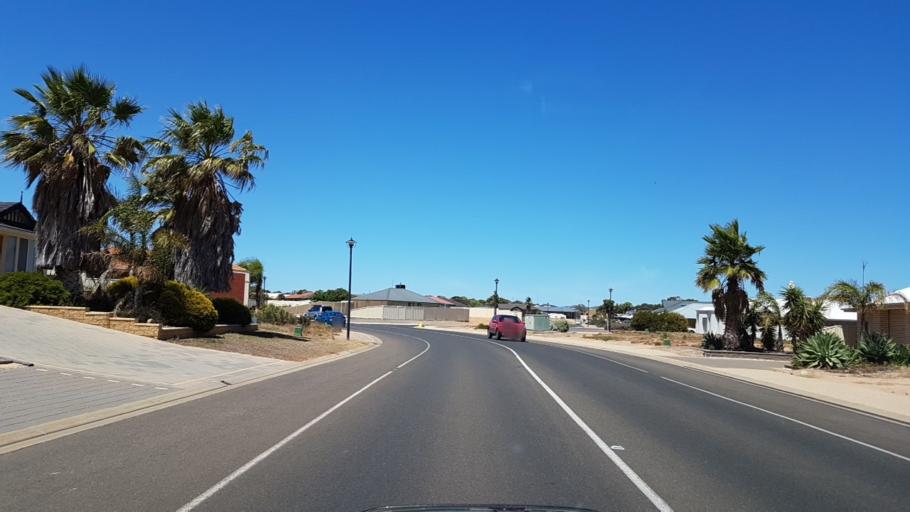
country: AU
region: South Australia
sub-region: Copper Coast
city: Wallaroo
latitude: -33.9199
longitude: 137.6424
